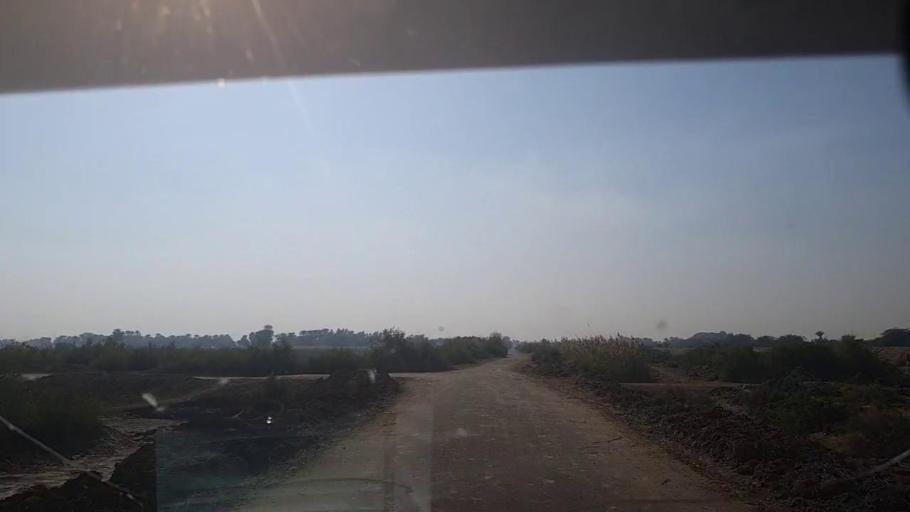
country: PK
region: Sindh
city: Gambat
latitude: 27.3812
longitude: 68.5832
